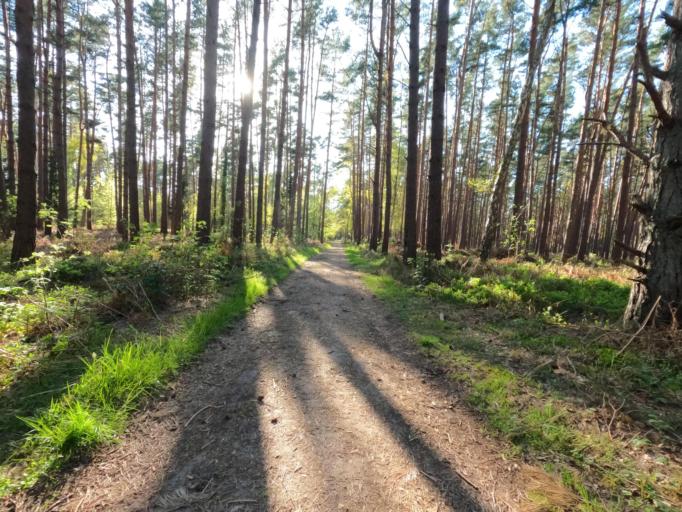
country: DE
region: Mecklenburg-Vorpommern
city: Born
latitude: 54.3953
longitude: 12.5315
